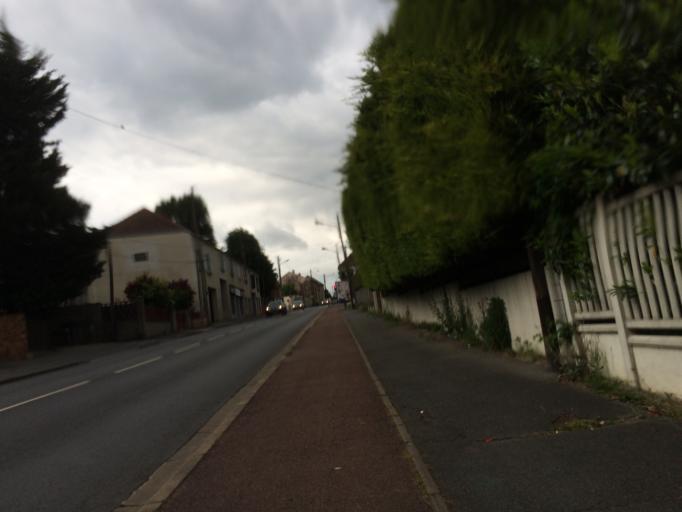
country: FR
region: Ile-de-France
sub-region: Departement de l'Essonne
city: Epinay-sur-Orge
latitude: 48.6819
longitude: 2.3123
